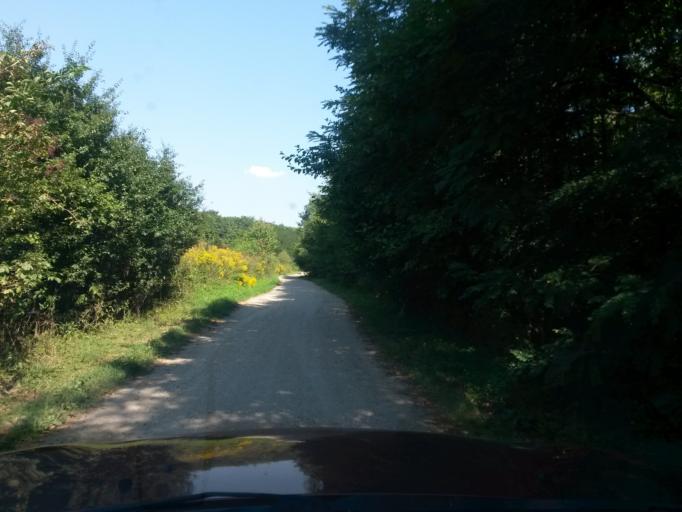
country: HU
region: Borsod-Abauj-Zemplen
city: Gonc
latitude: 48.5167
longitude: 21.2063
